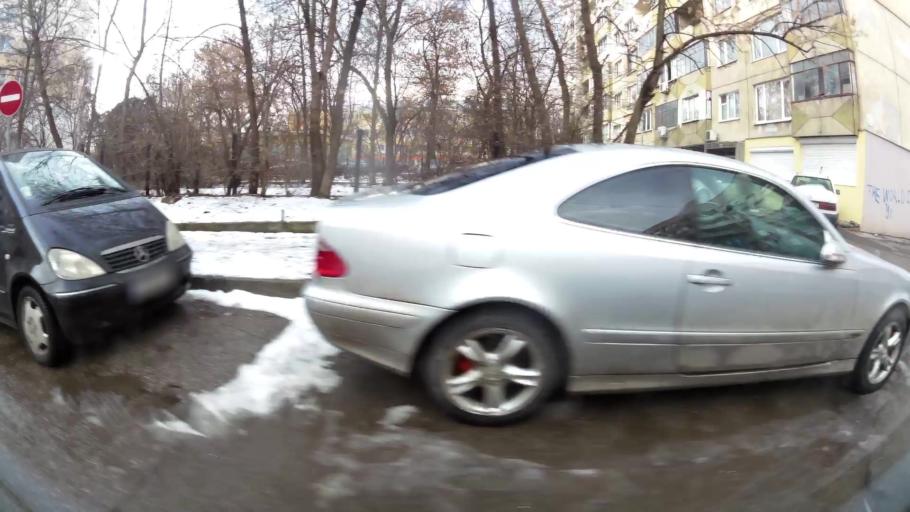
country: BG
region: Sofia-Capital
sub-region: Stolichna Obshtina
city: Sofia
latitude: 42.7002
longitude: 23.2926
